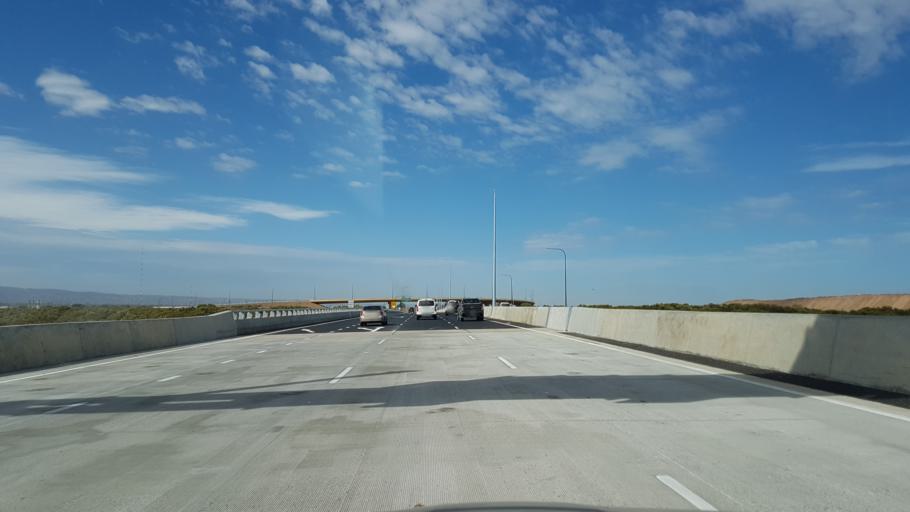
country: AU
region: South Australia
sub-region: Port Adelaide Enfield
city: Blair Athol
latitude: -34.8237
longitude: 138.5624
